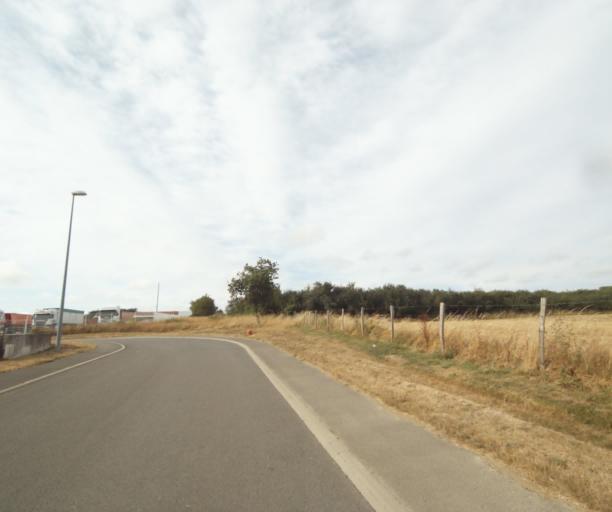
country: FR
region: Pays de la Loire
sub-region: Departement de la Vendee
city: Chateau-d'Olonne
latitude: 46.4947
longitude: -1.7299
